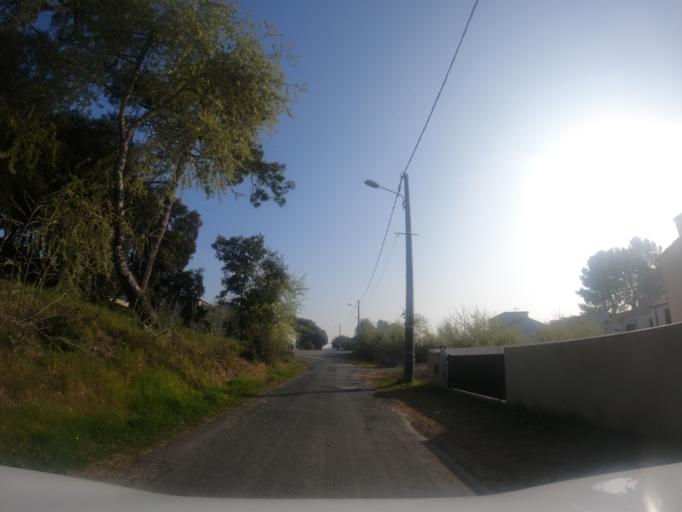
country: FR
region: Pays de la Loire
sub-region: Departement de la Vendee
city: La Tranche-sur-Mer
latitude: 46.3490
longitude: -1.4477
